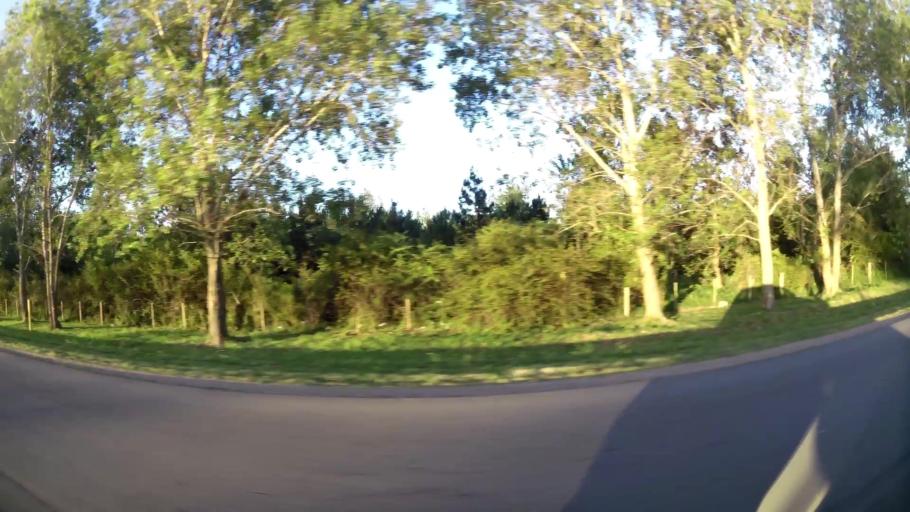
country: UY
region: Canelones
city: Barra de Carrasco
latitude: -34.8438
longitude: -56.0115
